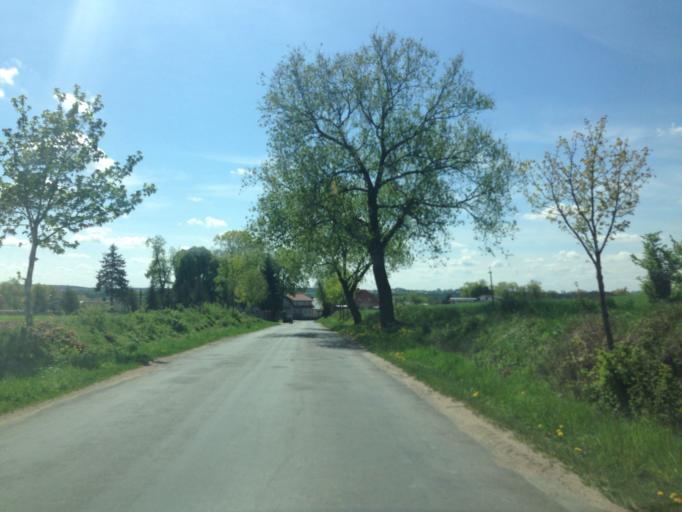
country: PL
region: Kujawsko-Pomorskie
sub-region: Powiat brodnicki
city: Bartniczka
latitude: 53.2593
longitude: 19.6373
